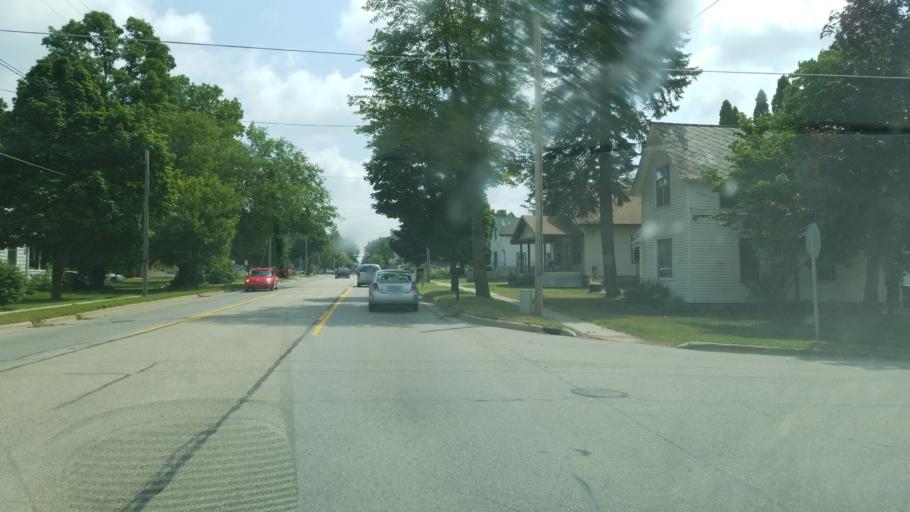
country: US
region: Michigan
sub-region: Kent County
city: Cedar Springs
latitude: 43.2200
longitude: -85.5538
